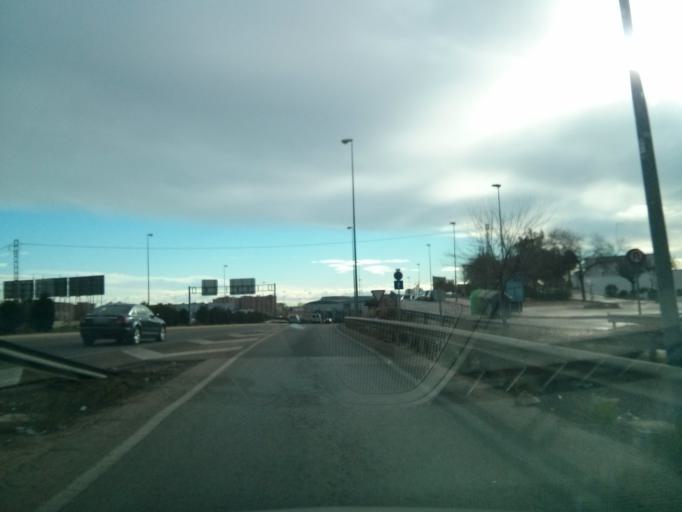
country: ES
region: Valencia
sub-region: Provincia de Valencia
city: Paterna
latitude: 39.5096
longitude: -0.4415
